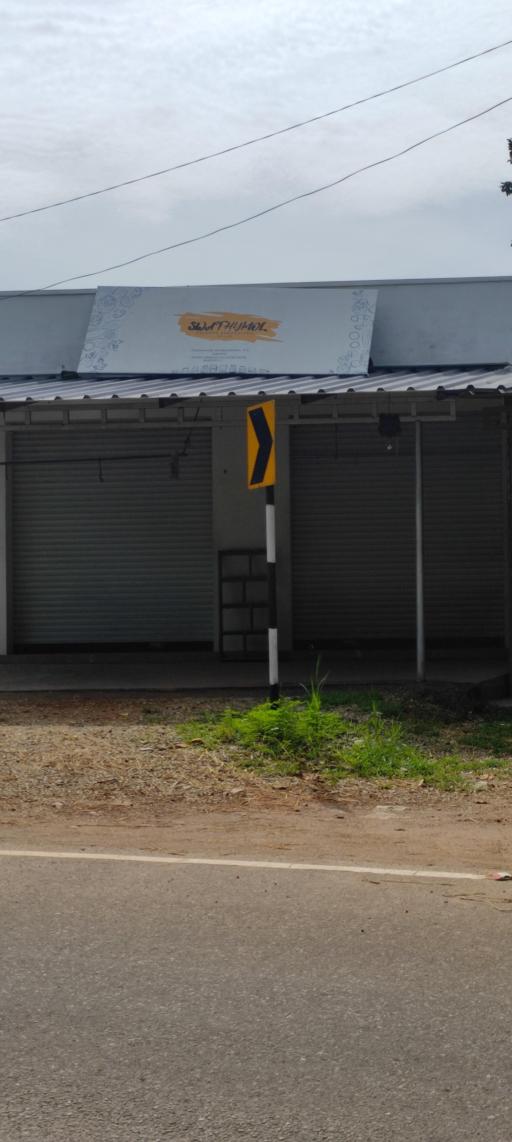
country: IN
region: Kerala
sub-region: Thiruvananthapuram
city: Nedumangad
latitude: 8.6340
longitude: 77.0732
